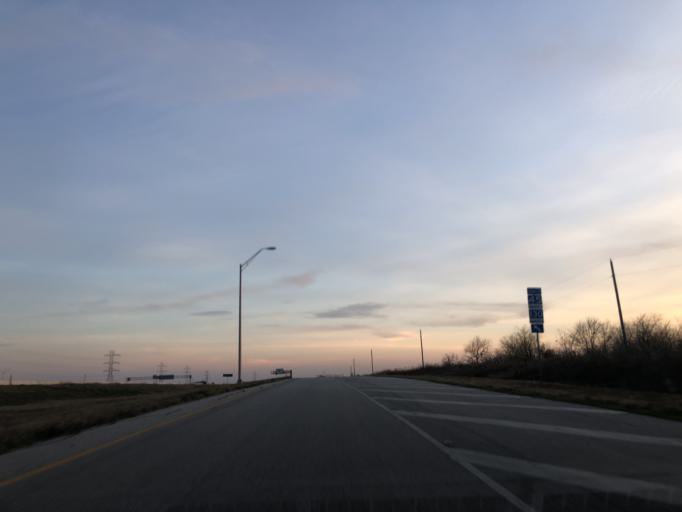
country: US
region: Texas
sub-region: Travis County
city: Pflugerville
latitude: 30.4037
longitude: -97.5835
